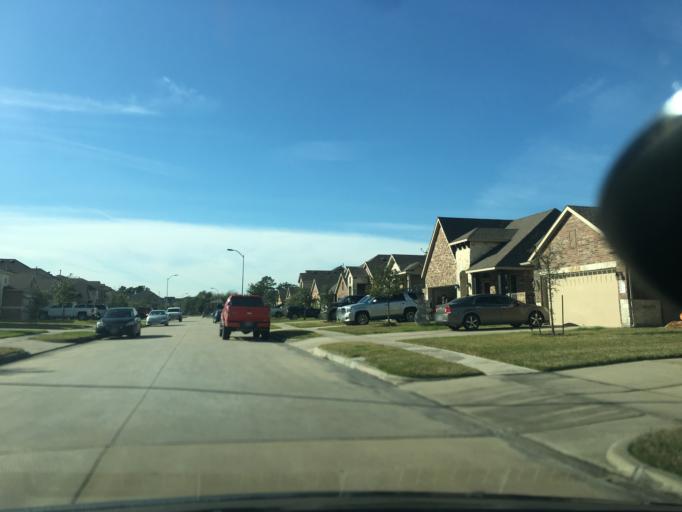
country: US
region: Texas
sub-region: Harris County
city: Cloverleaf
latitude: 29.8155
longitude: -95.1585
